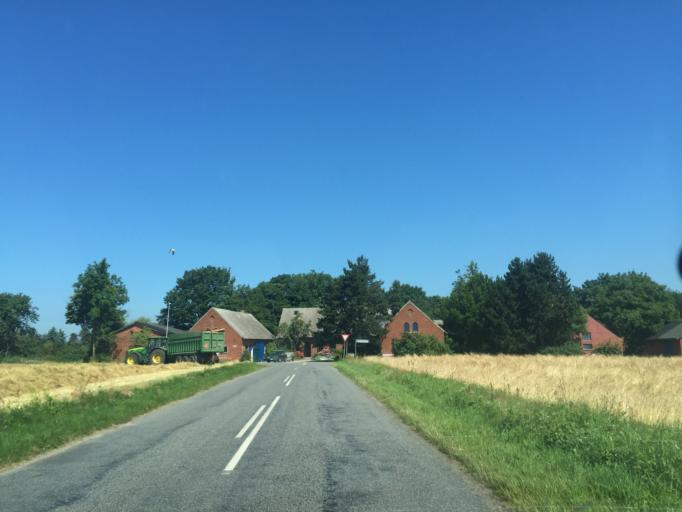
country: DK
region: South Denmark
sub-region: Nordfyns Kommune
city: Otterup
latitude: 55.5918
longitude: 10.3699
